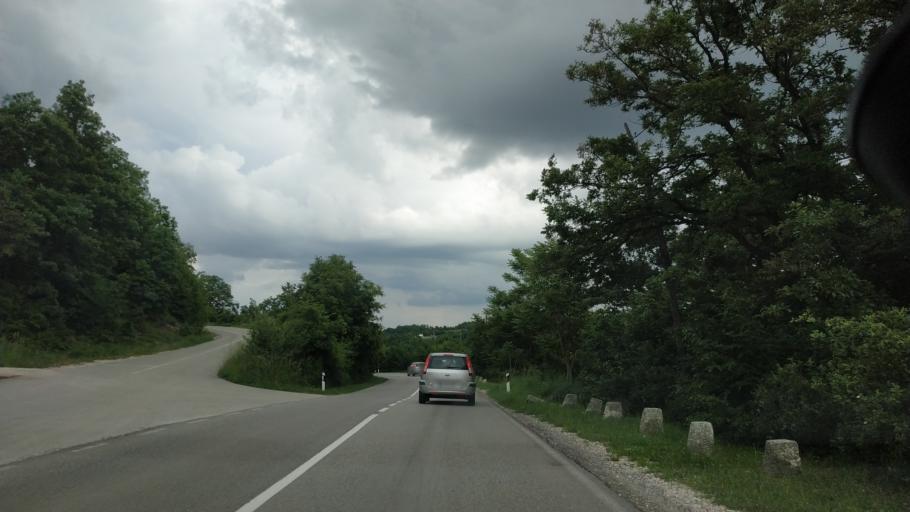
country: RS
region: Central Serbia
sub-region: Borski Okrug
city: Bor
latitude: 44.0489
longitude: 22.0755
